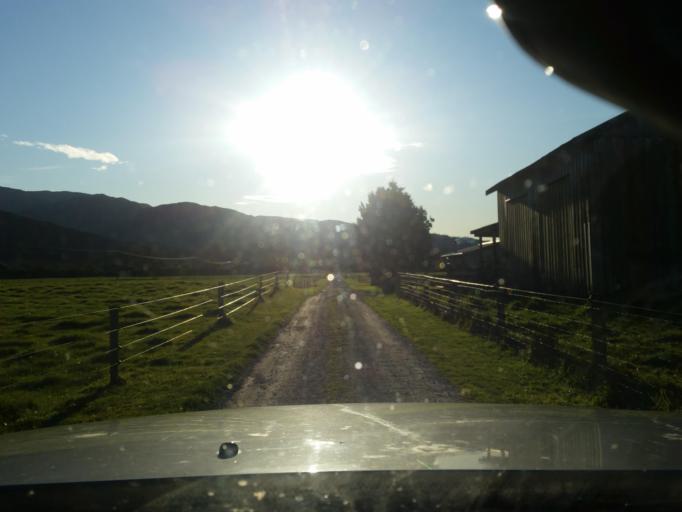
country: NZ
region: Tasman
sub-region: Tasman District
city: Takaka
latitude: -40.8777
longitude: 172.7989
